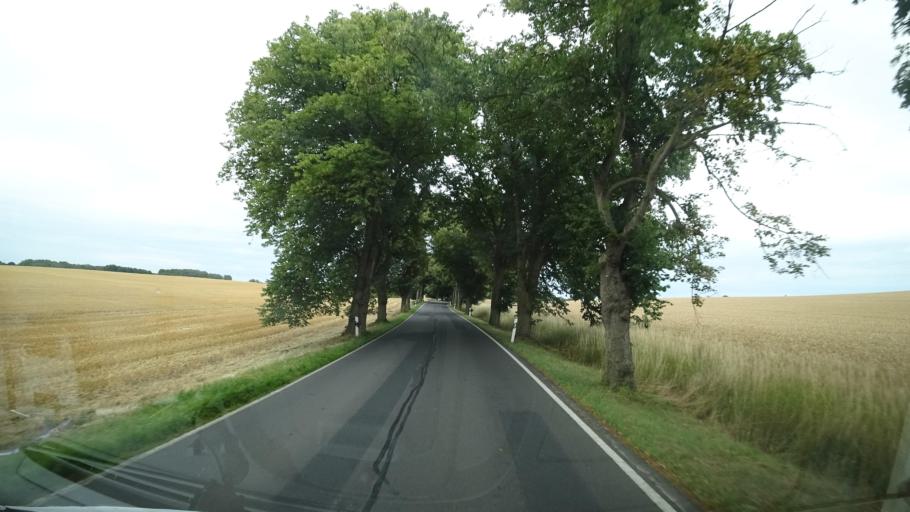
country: DE
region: Mecklenburg-Vorpommern
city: Poseritz
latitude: 54.3031
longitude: 13.2443
